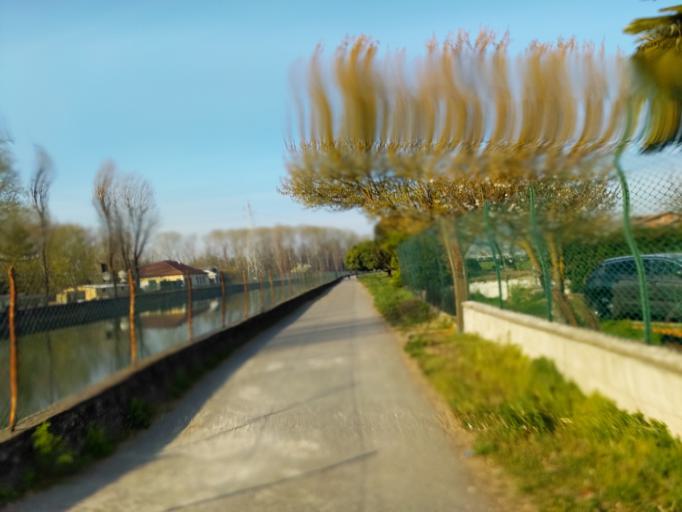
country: IT
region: Piedmont
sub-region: Provincia di Torino
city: San Mauro Torinese
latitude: 45.0949
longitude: 7.7372
